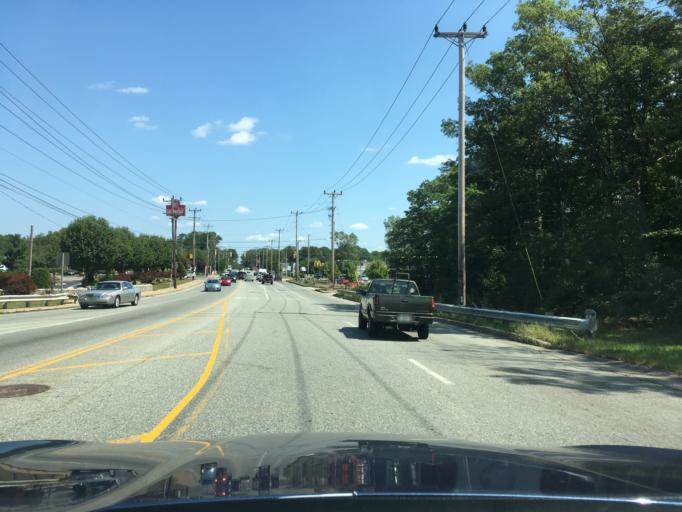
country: US
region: Rhode Island
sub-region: Kent County
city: West Warwick
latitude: 41.6604
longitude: -71.5464
